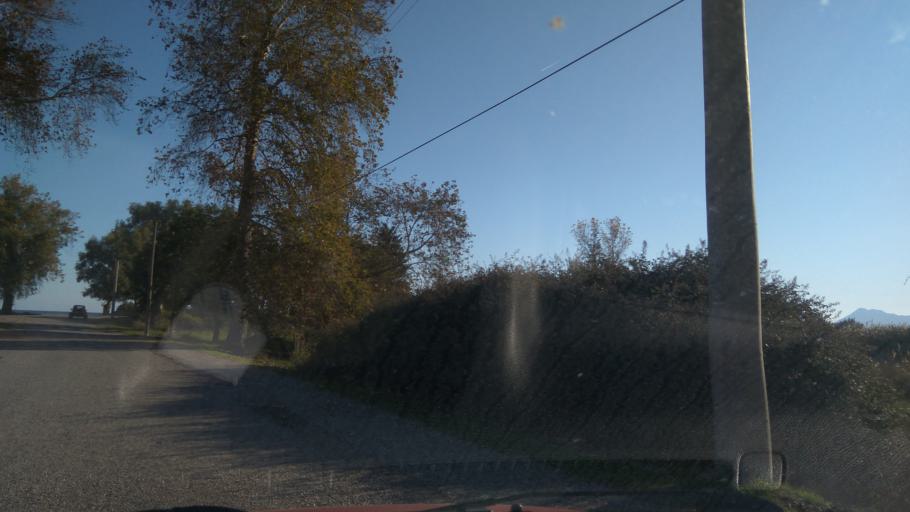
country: TR
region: Antalya
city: Kemer
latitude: 36.5618
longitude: 30.5718
